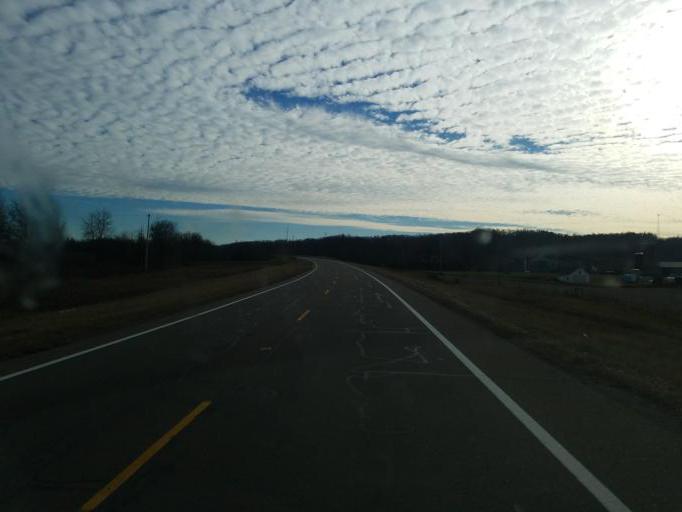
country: US
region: Ohio
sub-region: Muskingum County
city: Dresden
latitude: 40.1457
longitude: -82.0301
